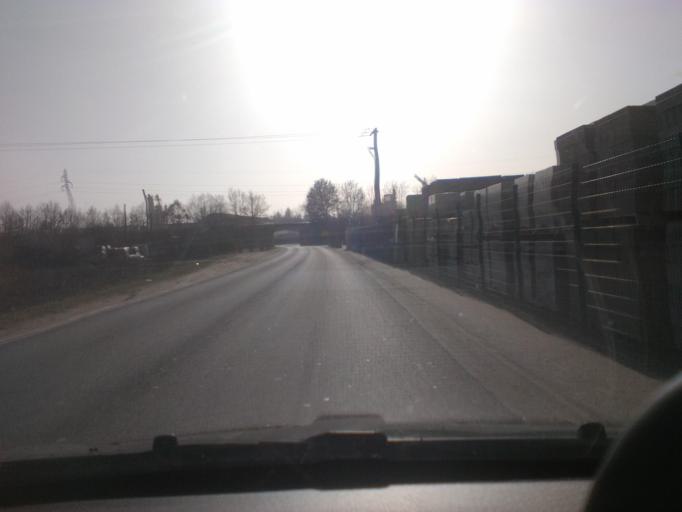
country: FR
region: Lorraine
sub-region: Departement des Vosges
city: Sainte-Marguerite
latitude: 48.2675
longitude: 6.9744
